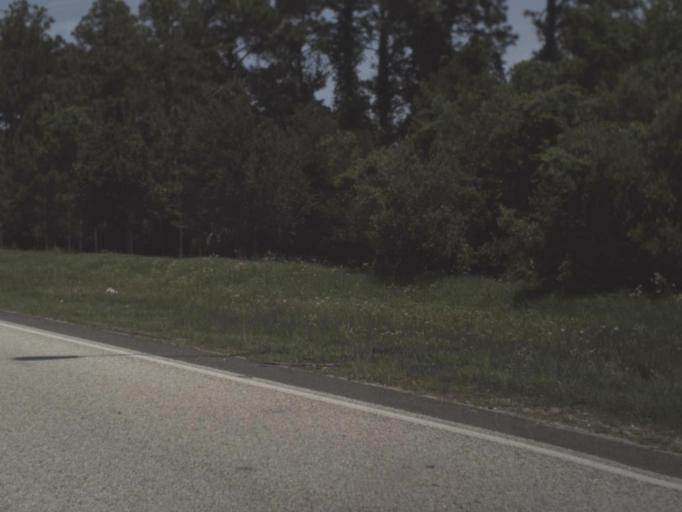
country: US
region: Florida
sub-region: Duval County
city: Neptune Beach
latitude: 30.2913
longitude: -81.5217
